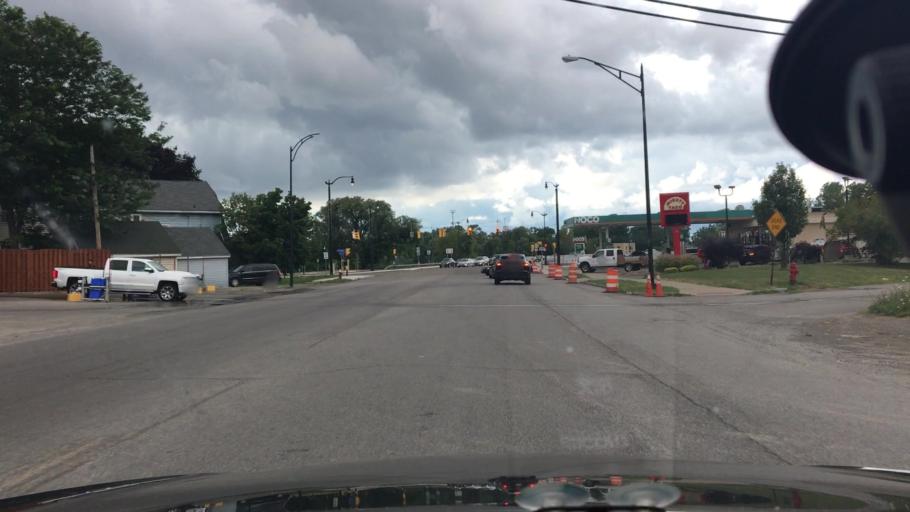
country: US
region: New York
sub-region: Erie County
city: West Seneca
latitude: 42.8589
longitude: -78.8250
